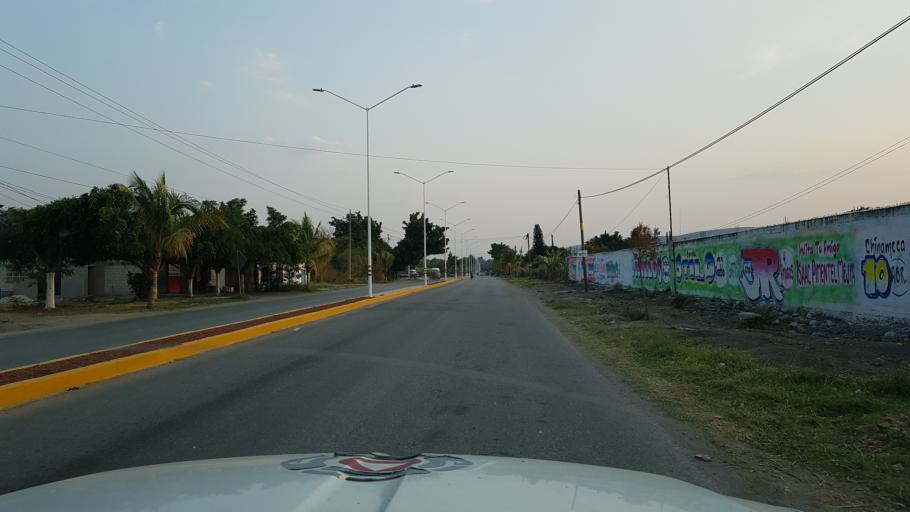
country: MX
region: Morelos
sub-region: Ayala
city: Abelardo L. Rodriguez
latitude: 18.7304
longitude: -98.9899
